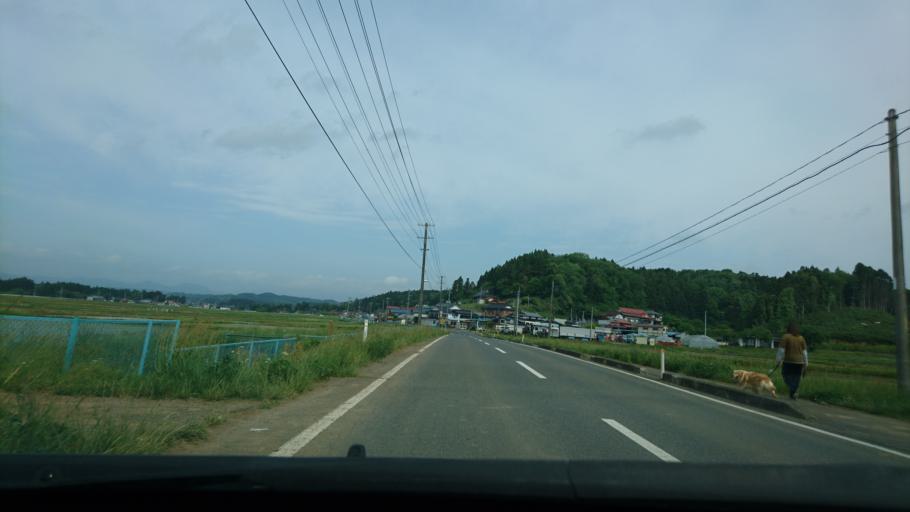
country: JP
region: Iwate
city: Ichinoseki
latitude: 38.8240
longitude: 141.0340
